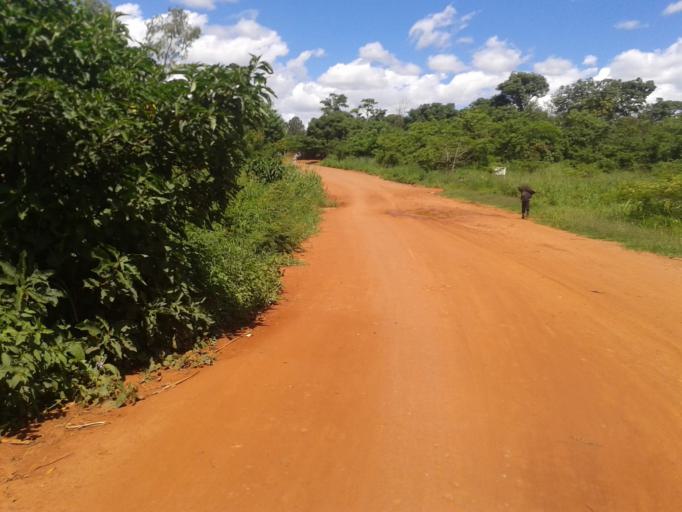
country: UG
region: Northern Region
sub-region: Gulu District
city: Gulu
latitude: 2.7634
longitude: 32.3205
